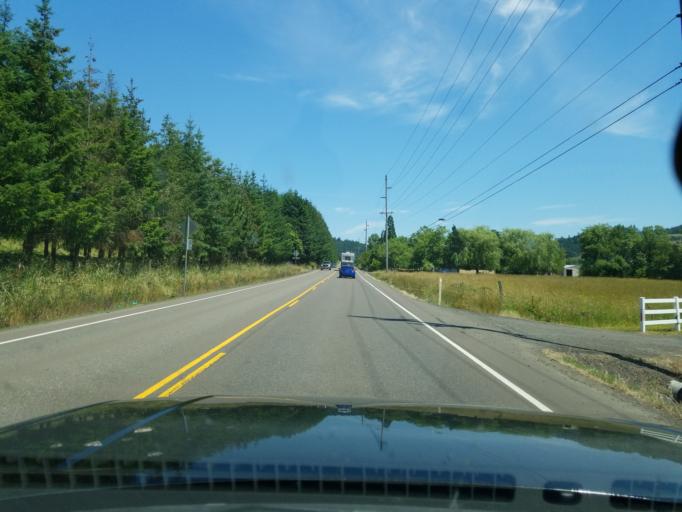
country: US
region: Oregon
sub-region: Yamhill County
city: Yamhill
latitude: 45.3629
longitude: -123.1678
